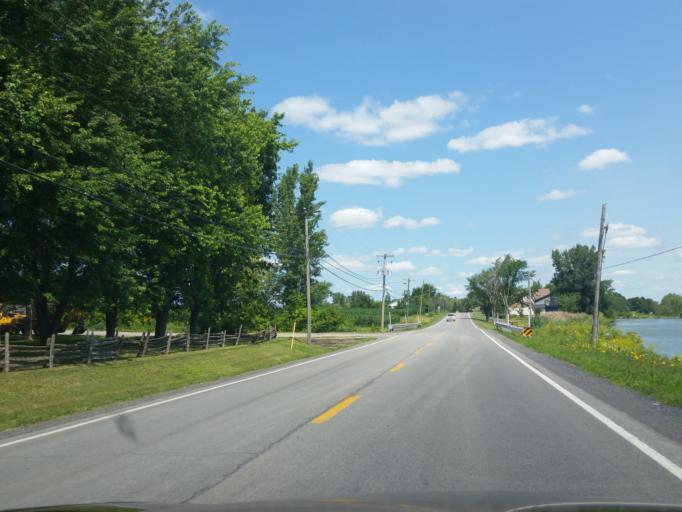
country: CA
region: Quebec
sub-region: Monteregie
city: Richelieu
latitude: 45.3943
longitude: -73.2602
